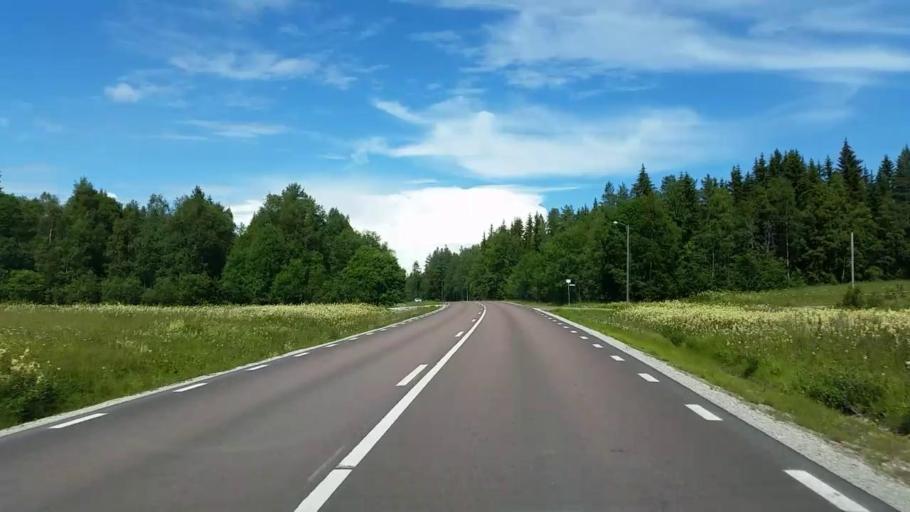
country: SE
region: Dalarna
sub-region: Rattviks Kommun
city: Raettvik
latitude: 61.0245
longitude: 15.2096
